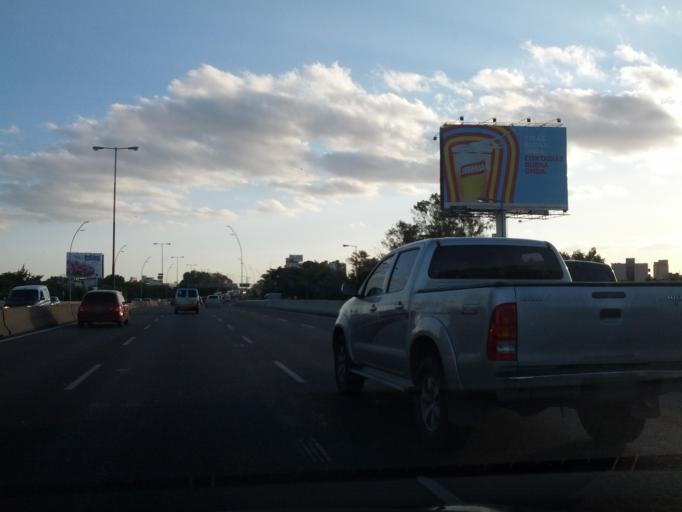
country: AR
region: Buenos Aires
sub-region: Partido de General San Martin
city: General San Martin
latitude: -34.5971
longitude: -58.5222
